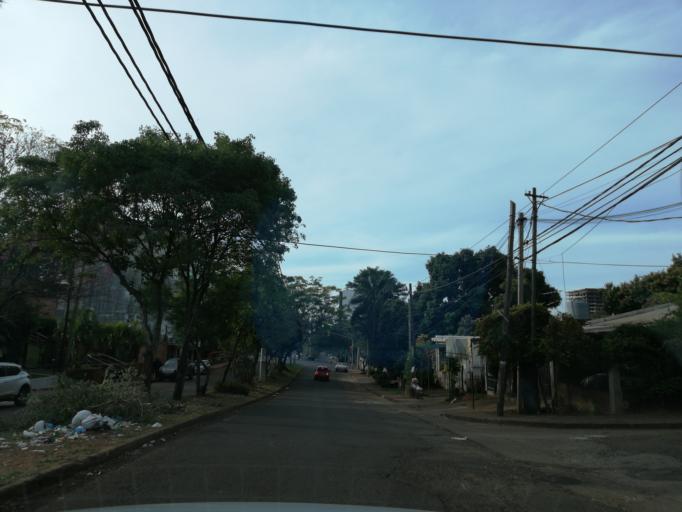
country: AR
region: Misiones
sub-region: Departamento de Capital
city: Posadas
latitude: -27.3636
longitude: -55.9122
